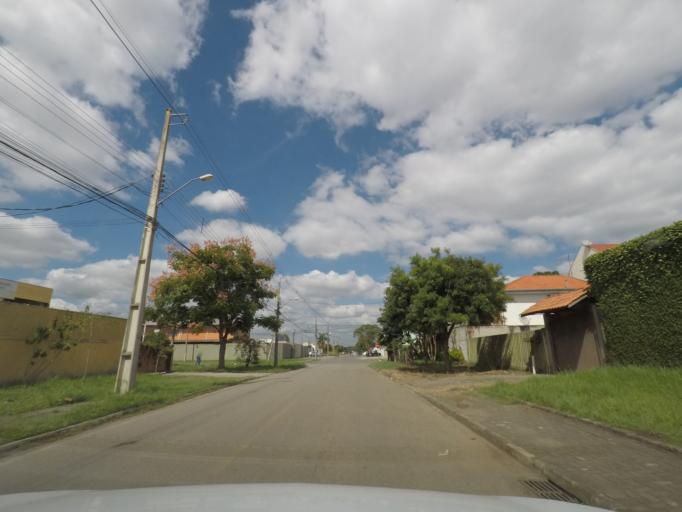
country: BR
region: Parana
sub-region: Sao Jose Dos Pinhais
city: Sao Jose dos Pinhais
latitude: -25.5061
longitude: -49.2182
